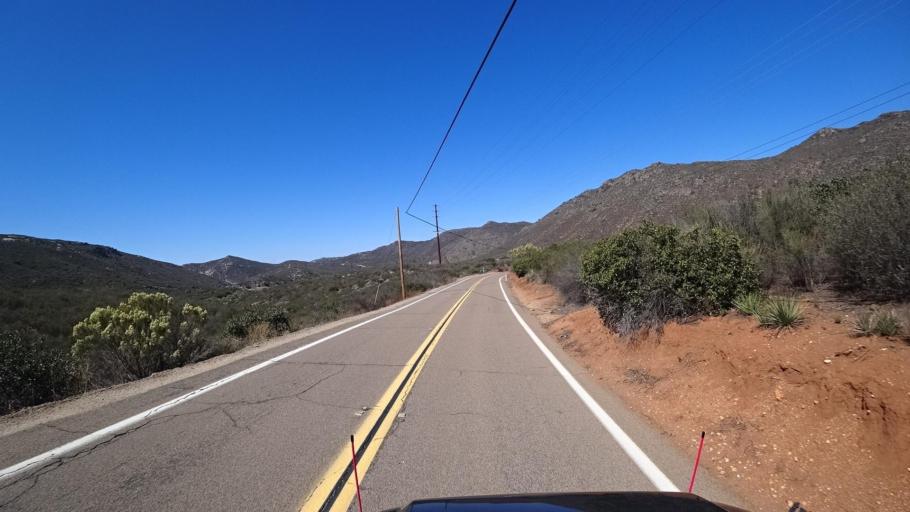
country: US
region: California
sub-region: San Diego County
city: Alpine
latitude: 32.7907
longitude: -116.7385
